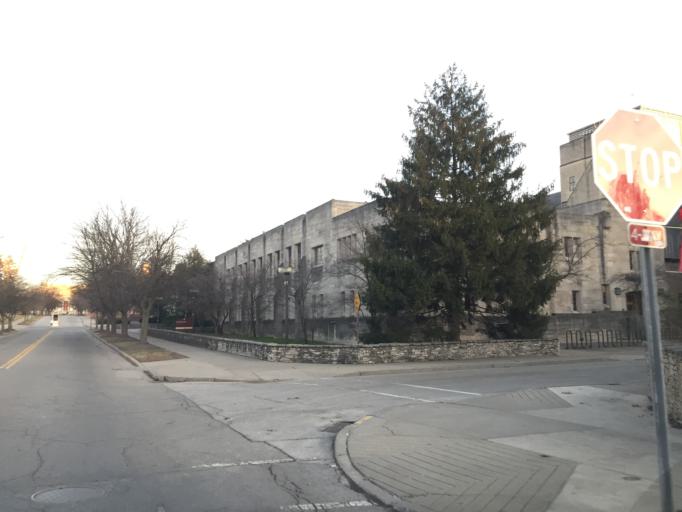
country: US
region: Indiana
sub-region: Monroe County
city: Bloomington
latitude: 39.1685
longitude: -86.5237
